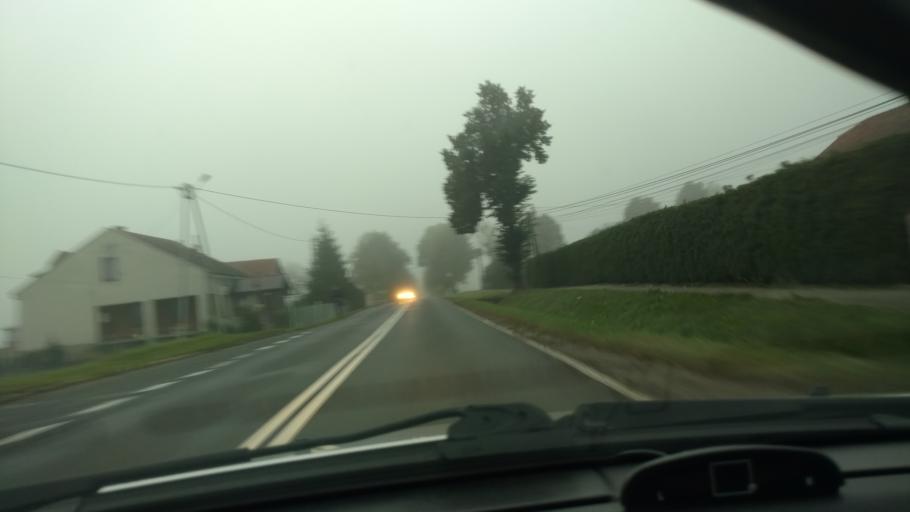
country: PL
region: Subcarpathian Voivodeship
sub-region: Powiat strzyzowski
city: Wisniowa
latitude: 49.8707
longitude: 21.6821
